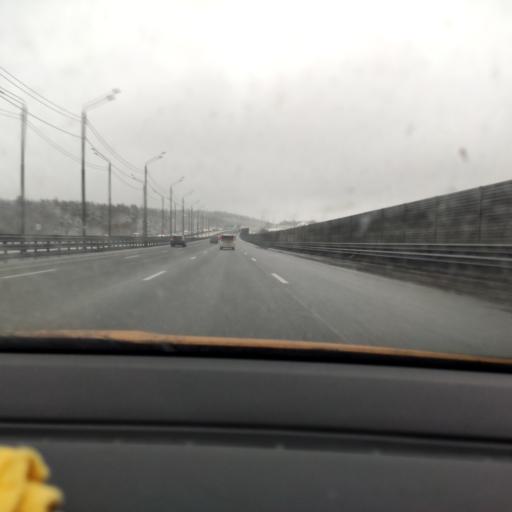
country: RU
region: Moskovskaya
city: Pavlovskaya Sloboda
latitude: 55.7877
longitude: 37.1177
